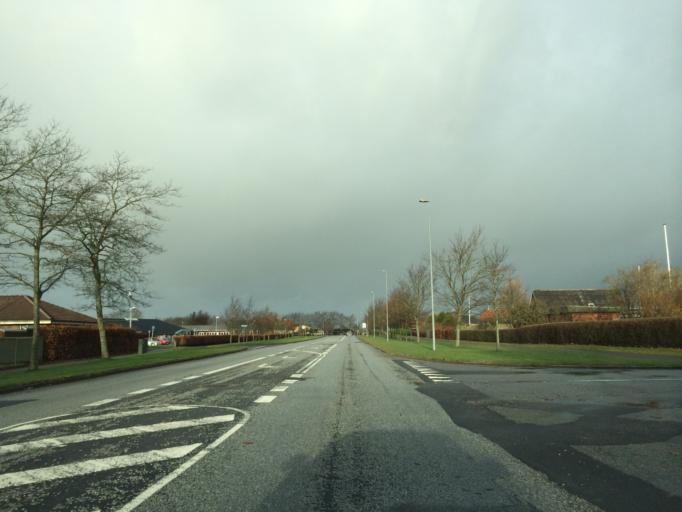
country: DK
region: Central Jutland
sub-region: Herning Kommune
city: Vildbjerg
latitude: 56.1913
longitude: 8.7623
